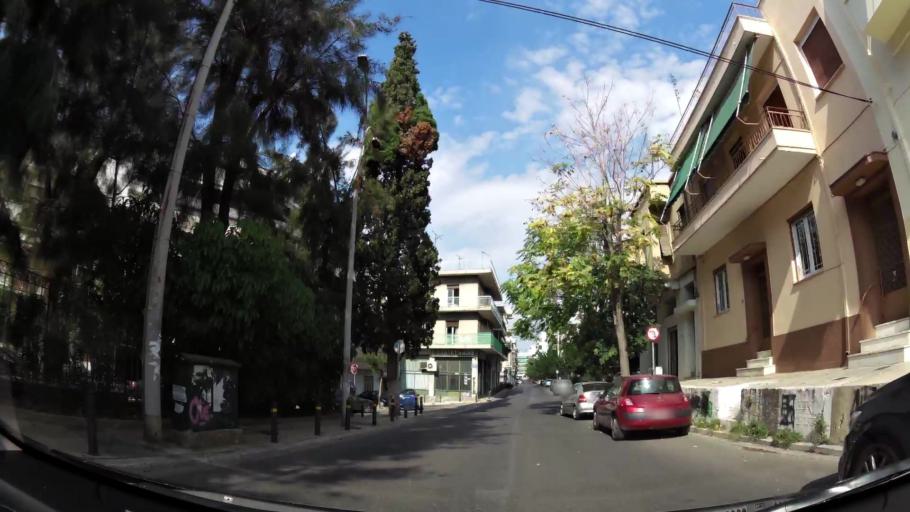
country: GR
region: Attica
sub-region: Nomarchia Athinas
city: Athens
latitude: 37.9998
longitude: 23.7150
